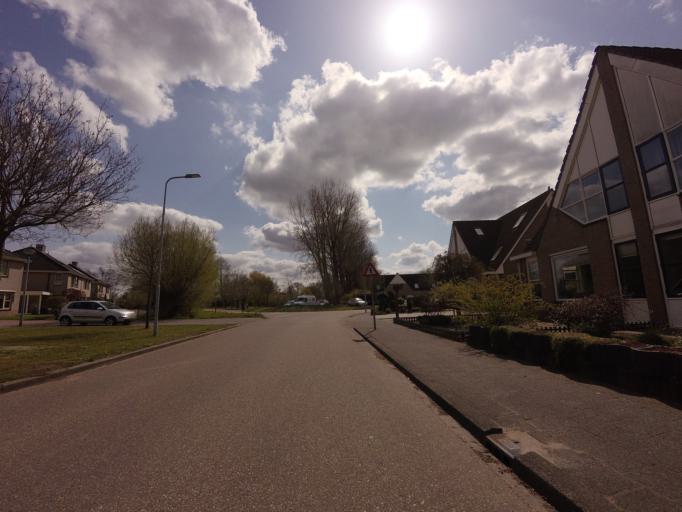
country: NL
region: Gelderland
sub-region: Gemeente Barneveld
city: Barneveld
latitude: 52.1393
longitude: 5.6081
